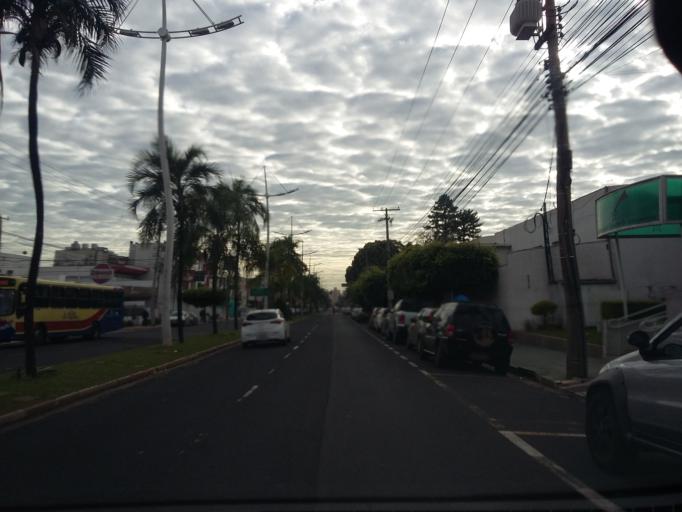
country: BR
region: Sao Paulo
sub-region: Sao Jose Do Rio Preto
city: Sao Jose do Rio Preto
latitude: -20.8318
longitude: -49.3988
